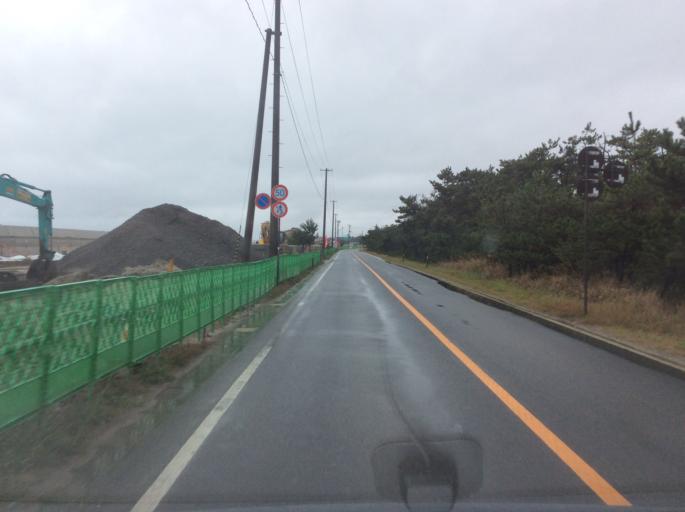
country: JP
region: Fukushima
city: Iwaki
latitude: 37.0939
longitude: 140.9844
